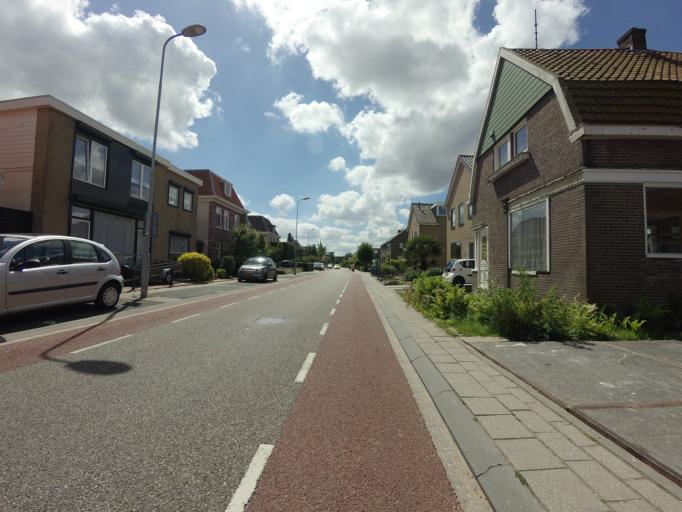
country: NL
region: North Holland
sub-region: Gemeente Landsmeer
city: Landsmeer
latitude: 52.4437
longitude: 4.8737
